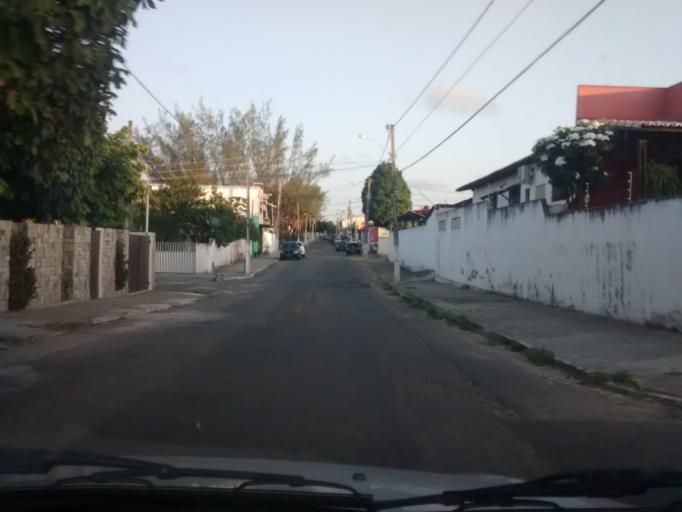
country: BR
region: Rio Grande do Norte
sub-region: Natal
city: Natal
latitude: -5.8717
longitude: -35.1874
